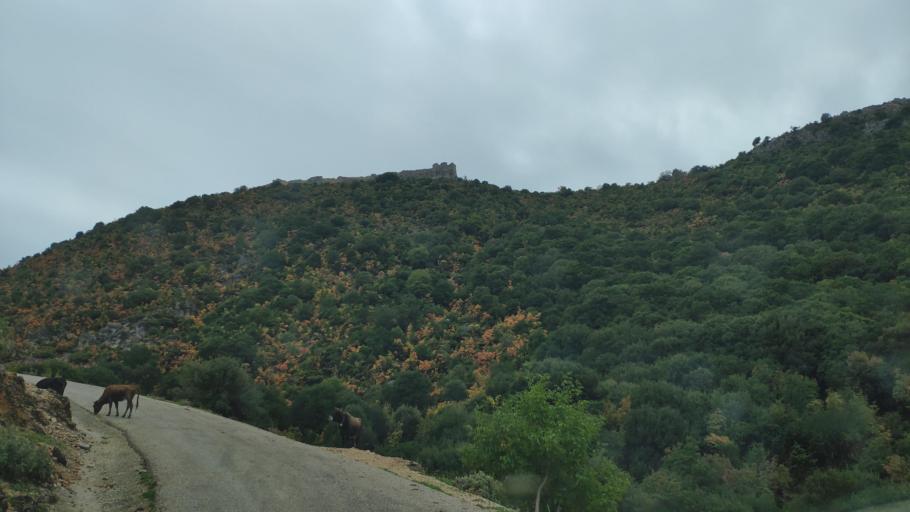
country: GR
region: Epirus
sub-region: Nomos Prevezis
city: Kanalaki
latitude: 39.3399
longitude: 20.6525
